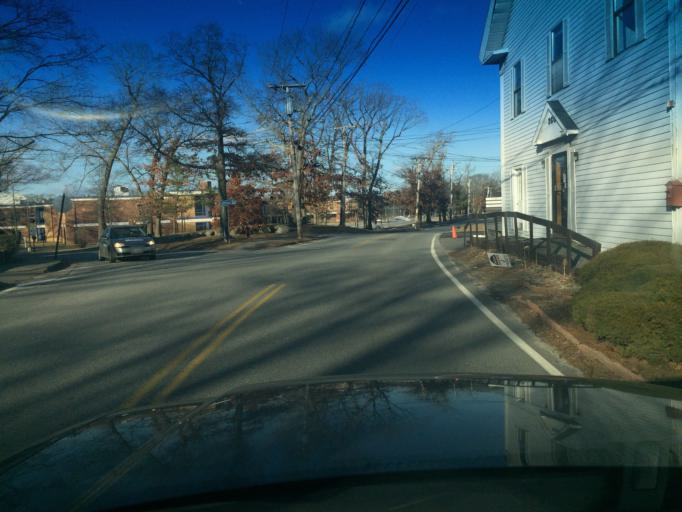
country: US
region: Massachusetts
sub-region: Middlesex County
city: Holliston
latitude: 42.2028
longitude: -71.4232
